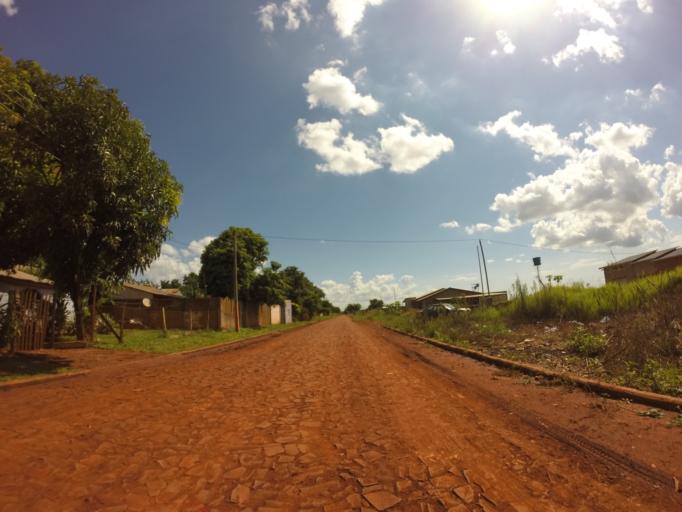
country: PY
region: Alto Parana
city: Ciudad del Este
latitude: -25.3732
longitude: -54.6530
